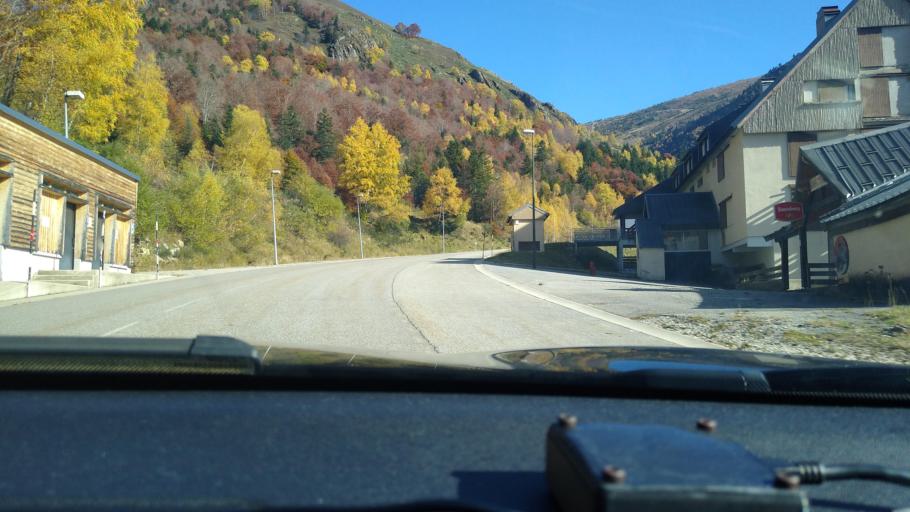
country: FR
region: Midi-Pyrenees
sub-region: Departement de l'Ariege
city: Ax-les-Thermes
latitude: 42.7313
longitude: 1.9541
